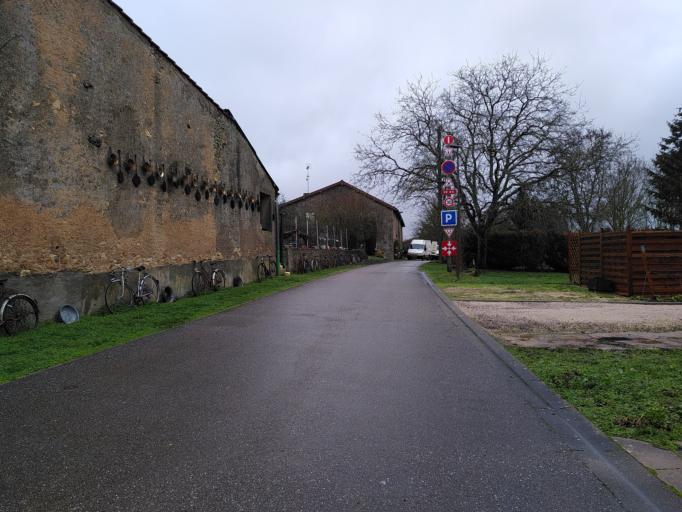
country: FR
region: Lorraine
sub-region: Departement de la Moselle
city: Gorze
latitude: 49.0105
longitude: 5.8627
